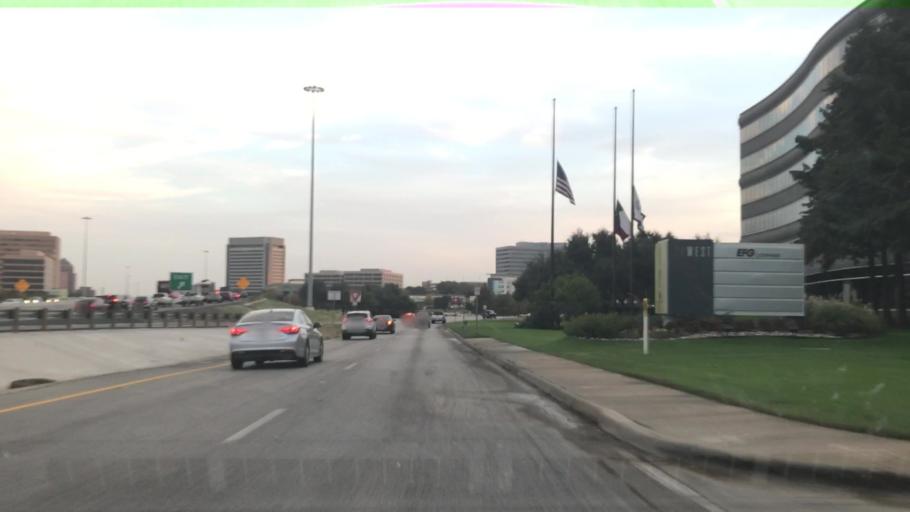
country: US
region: Texas
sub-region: Dallas County
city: Irving
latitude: 32.8706
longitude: -96.9458
